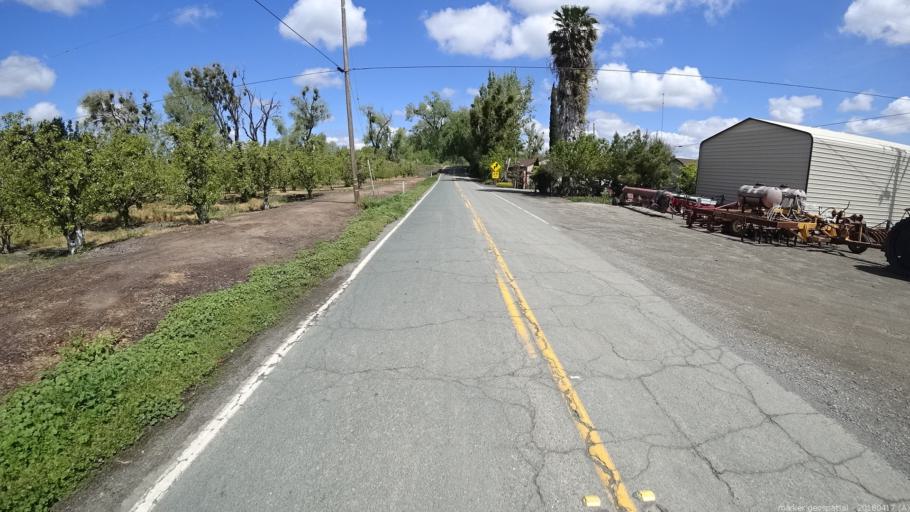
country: US
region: California
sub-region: Sacramento County
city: Walnut Grove
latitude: 38.2246
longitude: -121.5270
